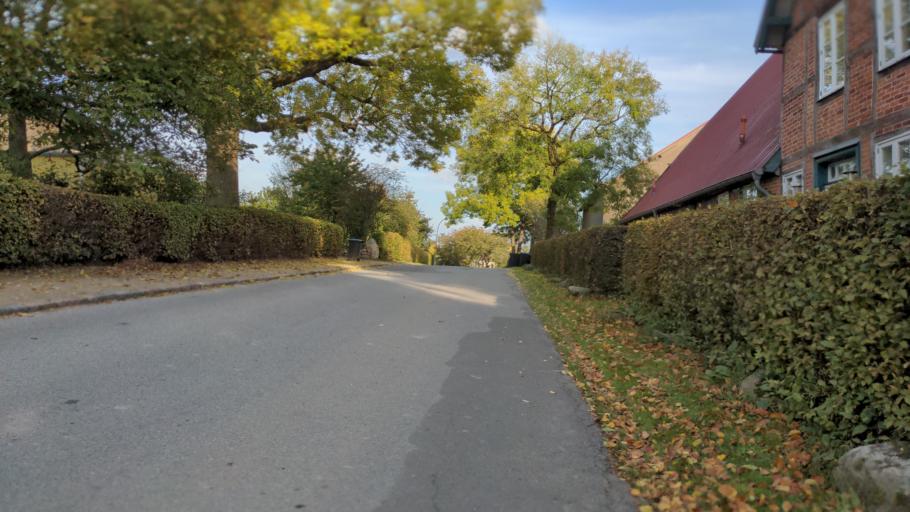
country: DE
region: Schleswig-Holstein
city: Ahrensbok
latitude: 53.9794
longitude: 10.5532
